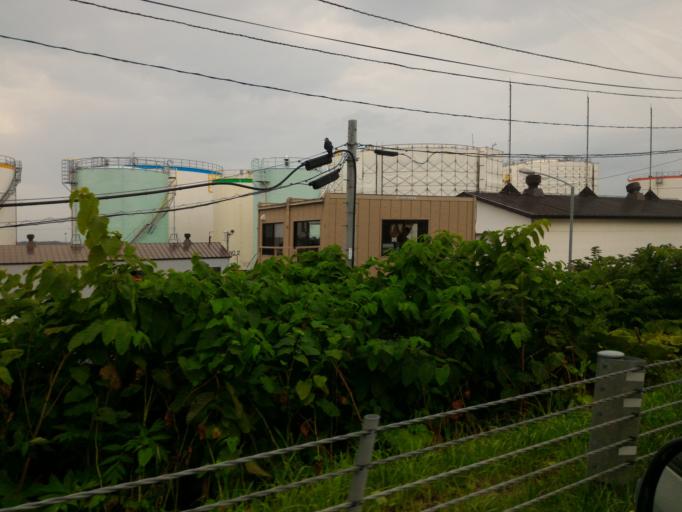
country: JP
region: Hokkaido
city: Rumoi
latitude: 43.9580
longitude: 141.6441
